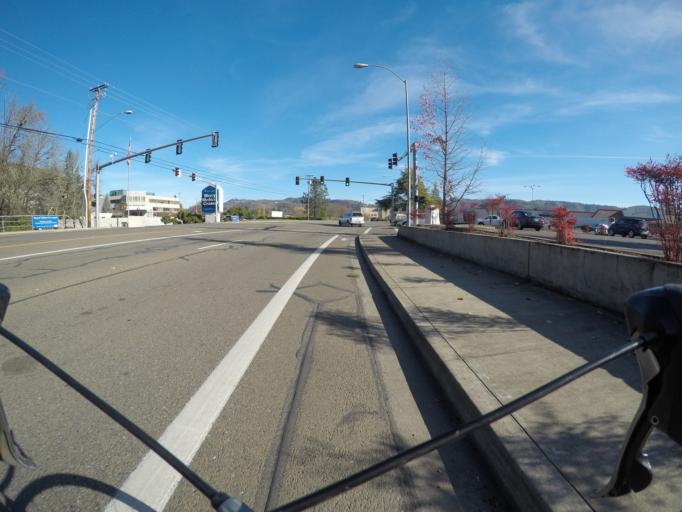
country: US
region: Oregon
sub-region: Douglas County
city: Roseburg
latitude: 43.2396
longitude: -123.3673
